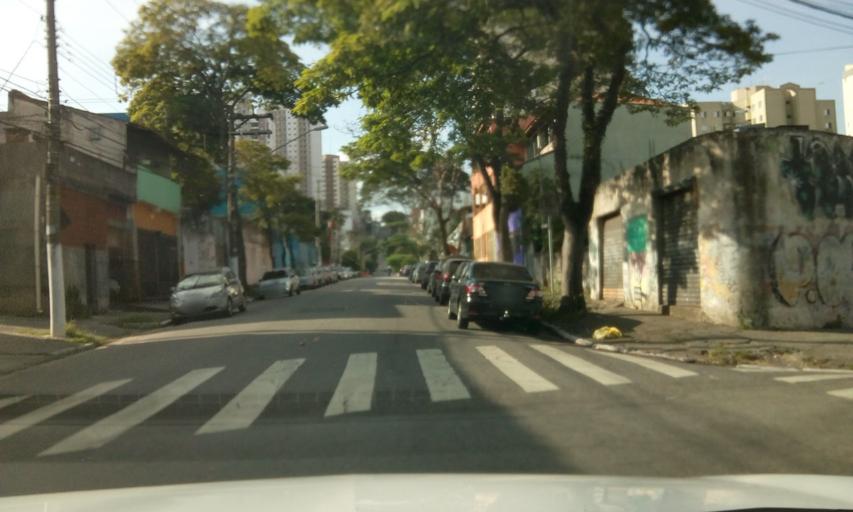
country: BR
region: Sao Paulo
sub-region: Sao Paulo
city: Sao Paulo
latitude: -23.5024
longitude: -46.6810
